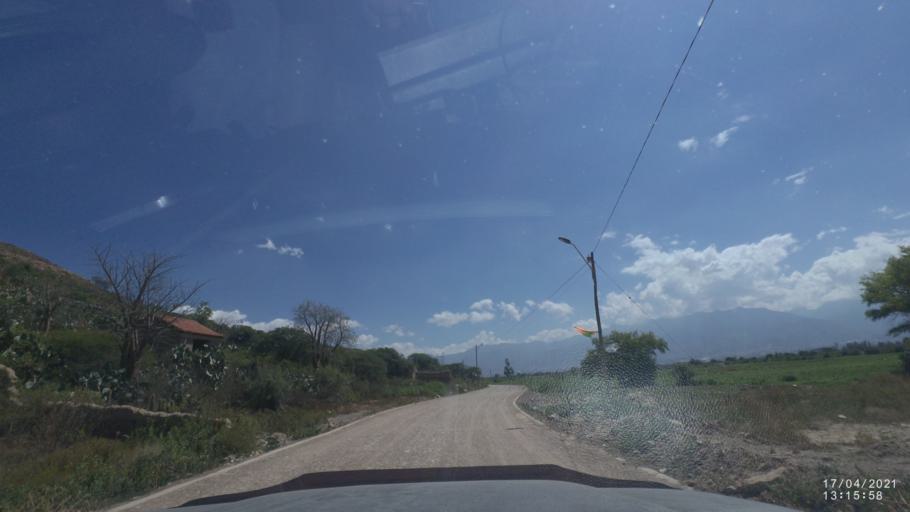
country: BO
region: Cochabamba
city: Cochabamba
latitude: -17.4179
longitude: -66.2339
